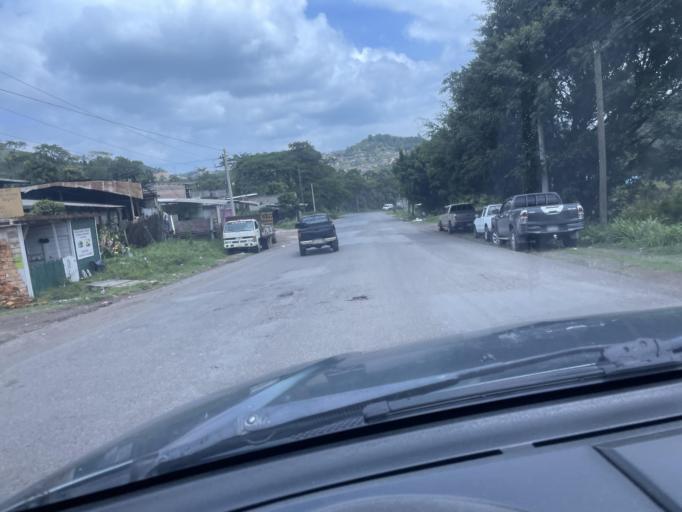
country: HN
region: Francisco Morazan
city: Rio Abajo
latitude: 14.1416
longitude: -87.2304
